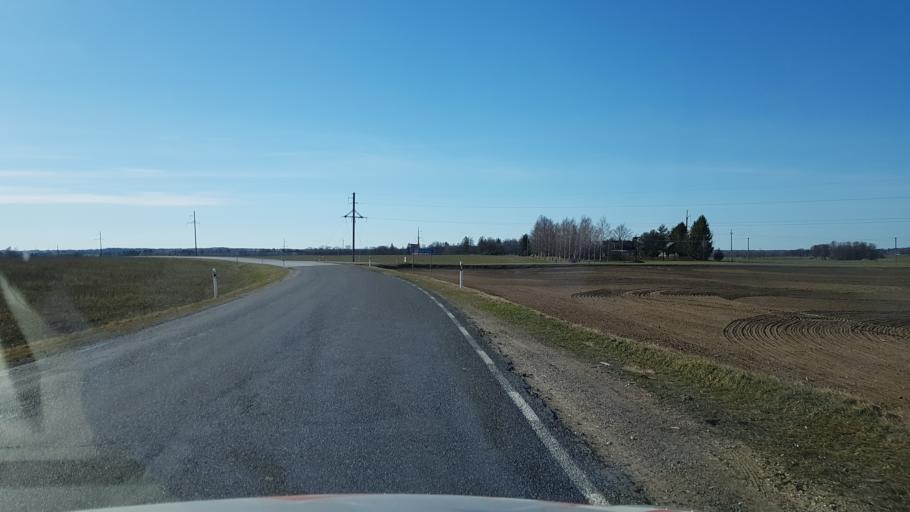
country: EE
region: Laeaene-Virumaa
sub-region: Vinni vald
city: Vinni
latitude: 59.3216
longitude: 26.5034
